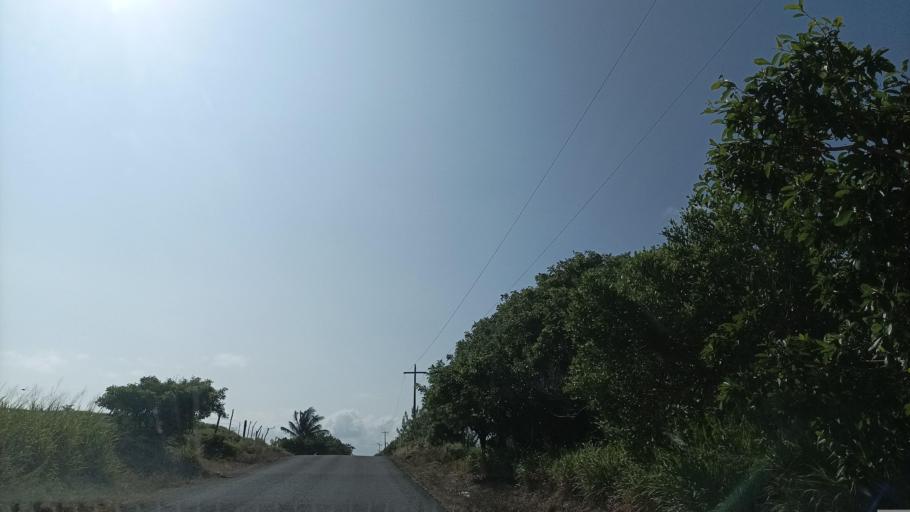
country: MX
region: Veracruz
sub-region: Pajapan
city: Pajapan
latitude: 18.2297
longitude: -94.6191
